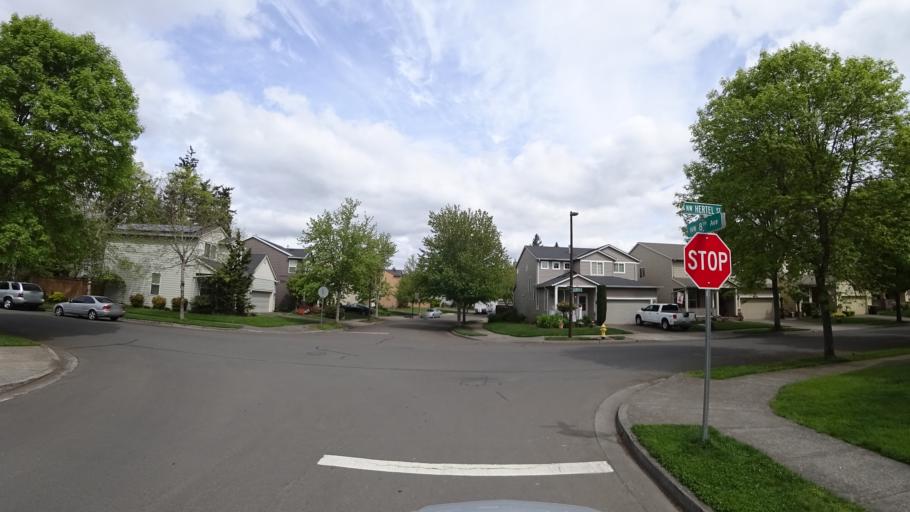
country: US
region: Oregon
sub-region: Washington County
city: Hillsboro
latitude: 45.5362
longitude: -122.9978
